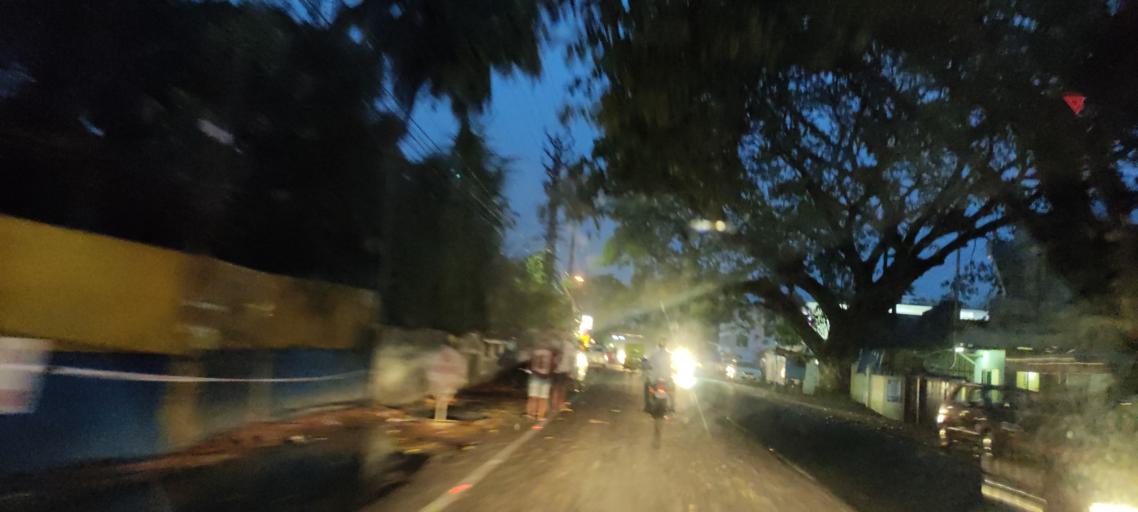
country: IN
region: Kerala
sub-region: Alappuzha
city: Arukutti
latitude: 9.8813
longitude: 76.3028
